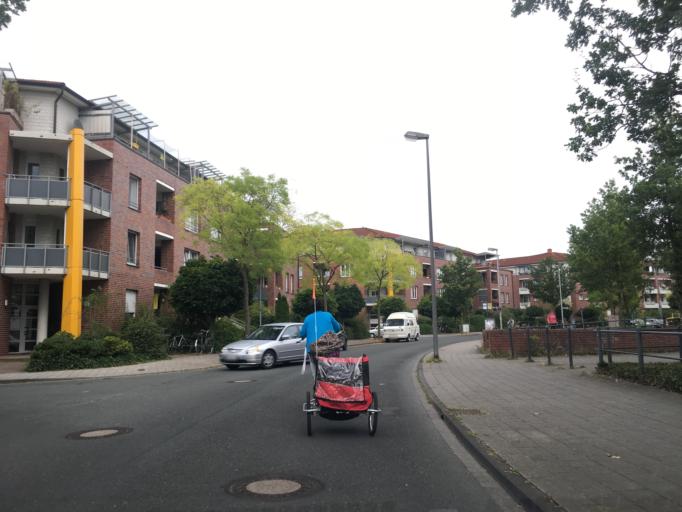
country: DE
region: North Rhine-Westphalia
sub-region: Regierungsbezirk Munster
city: Muenster
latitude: 51.9753
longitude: 7.5688
